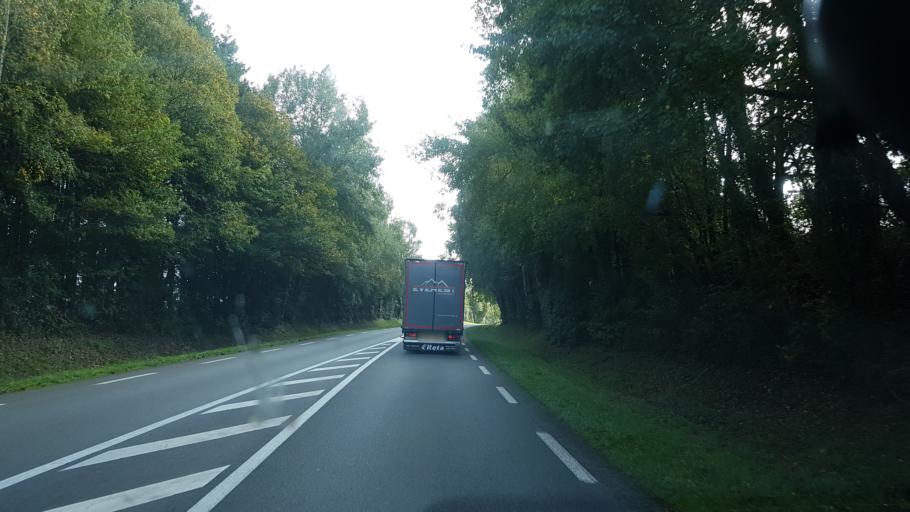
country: FR
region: Poitou-Charentes
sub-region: Departement de la Charente
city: Confolens
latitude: 46.0317
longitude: 0.6589
